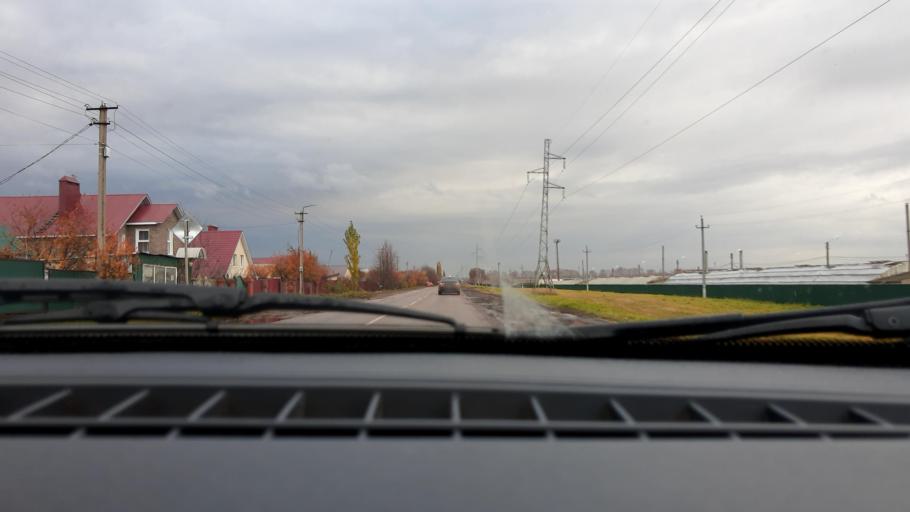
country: RU
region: Bashkortostan
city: Ufa
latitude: 54.8424
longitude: 55.9992
